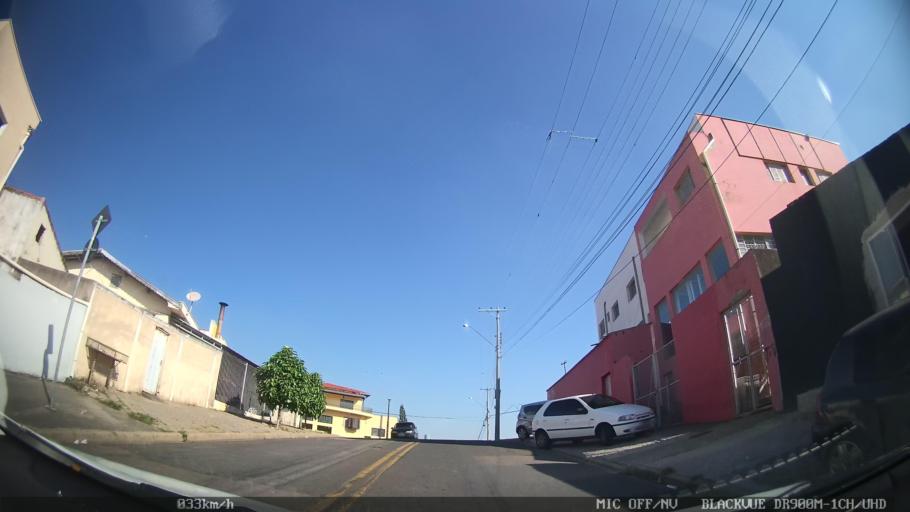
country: BR
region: Sao Paulo
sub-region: Campinas
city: Campinas
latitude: -22.9589
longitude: -47.0932
